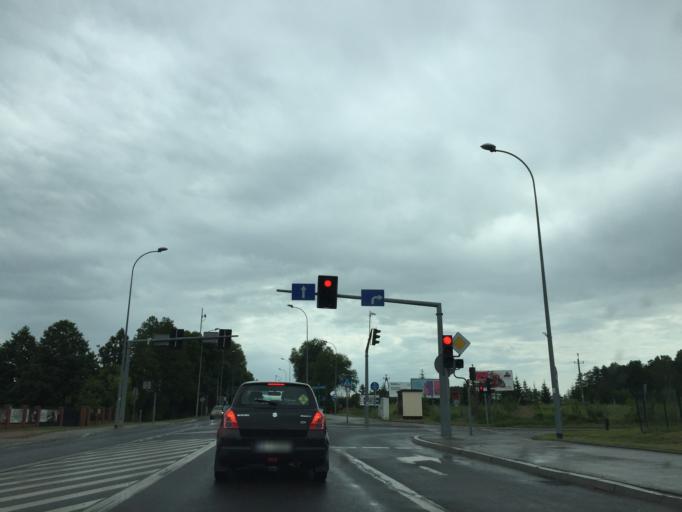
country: PL
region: Podlasie
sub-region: Bialystok
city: Bialystok
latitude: 53.0971
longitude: 23.2324
